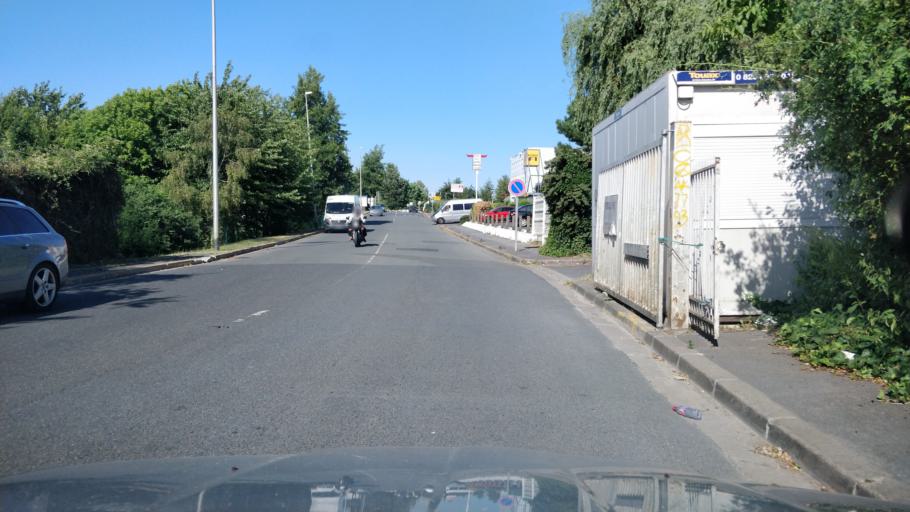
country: FR
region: Ile-de-France
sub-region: Departement de Seine-Saint-Denis
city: Villemomble
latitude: 48.8795
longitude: 2.4984
